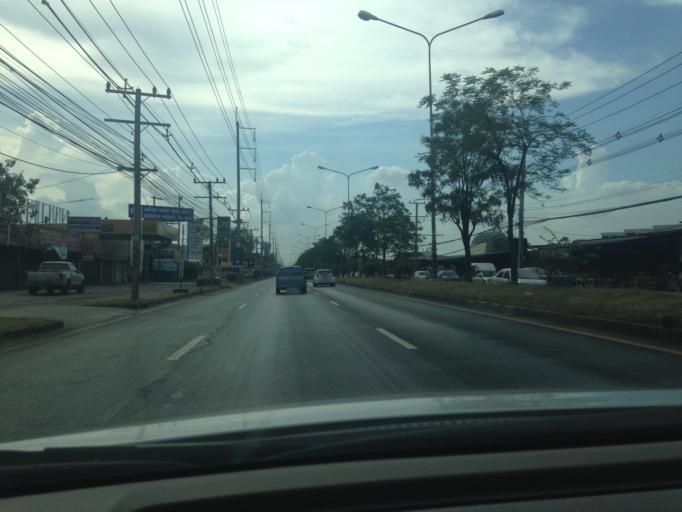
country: TH
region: Pathum Thani
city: Khlong Luang
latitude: 14.0660
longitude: 100.6680
